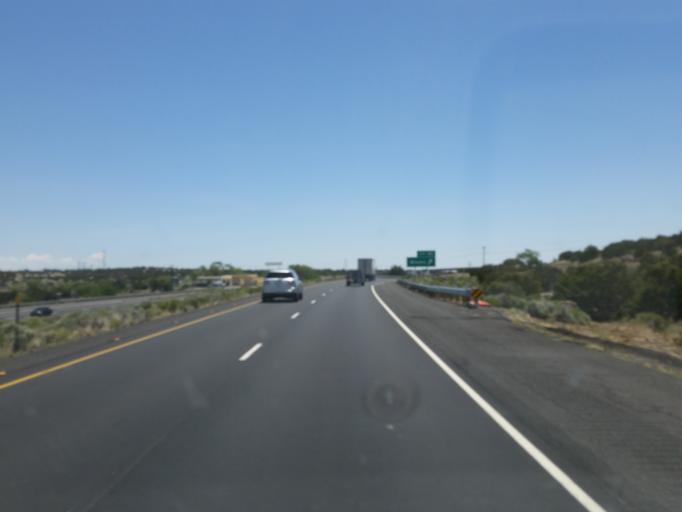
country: US
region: Arizona
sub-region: Coconino County
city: Flagstaff
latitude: 35.2025
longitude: -111.4129
